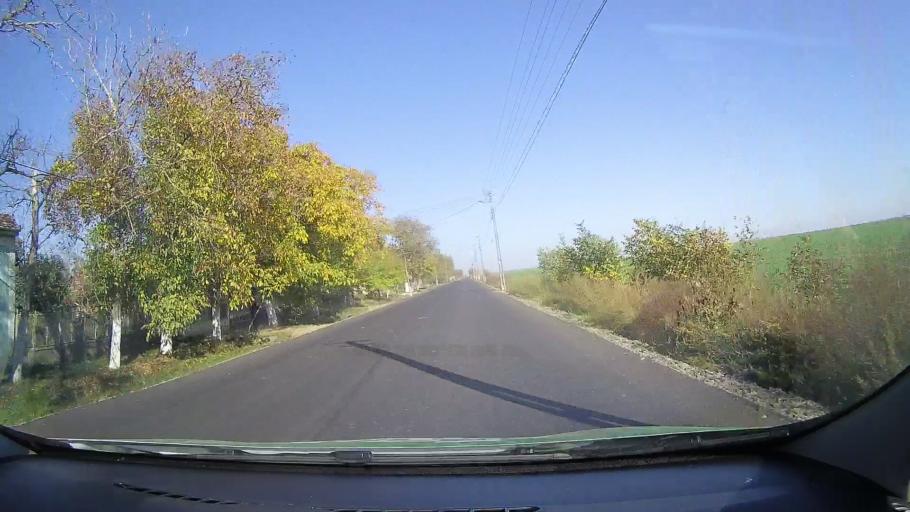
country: RO
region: Satu Mare
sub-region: Comuna Tiream
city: Tiream
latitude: 47.6215
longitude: 22.4682
